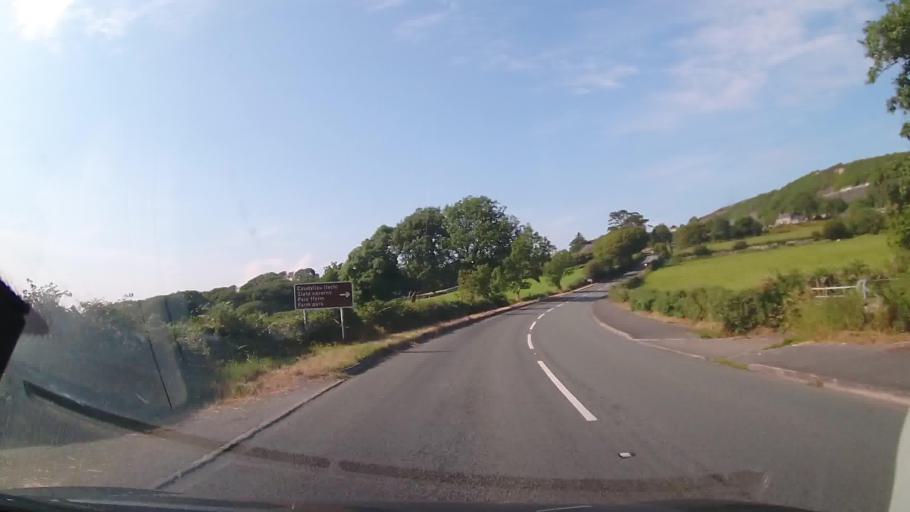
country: GB
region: Wales
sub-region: Gwynedd
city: Llanfair
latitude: 52.8348
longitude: -4.1138
